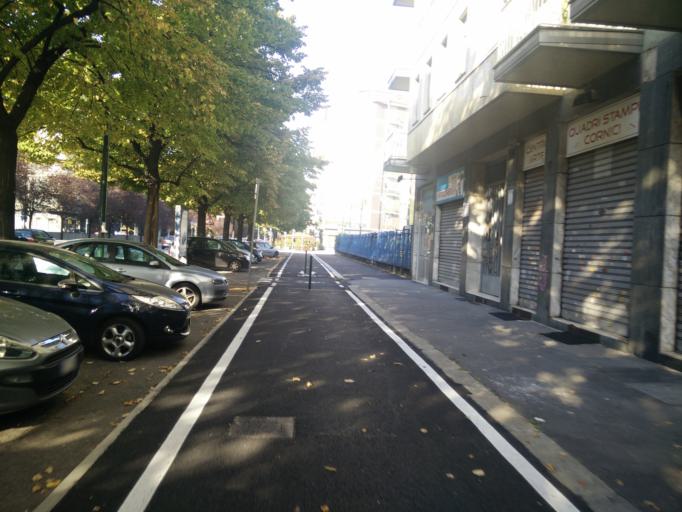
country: IT
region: Piedmont
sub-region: Provincia di Torino
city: Gerbido
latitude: 45.0383
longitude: 7.6308
